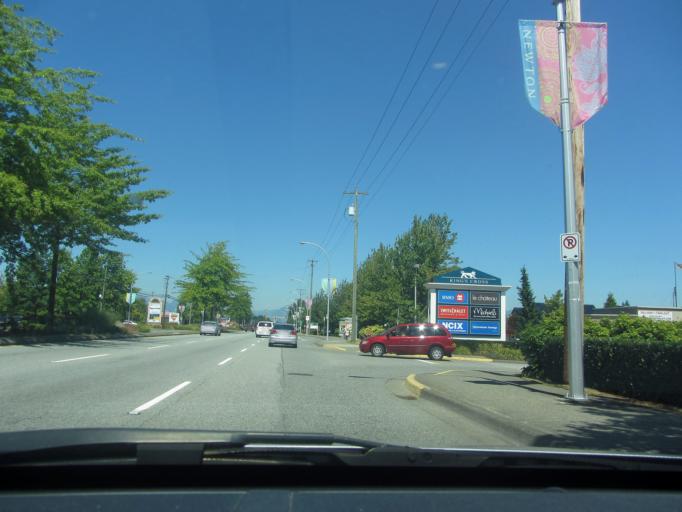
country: CA
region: British Columbia
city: Surrey
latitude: 49.1384
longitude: -122.8455
